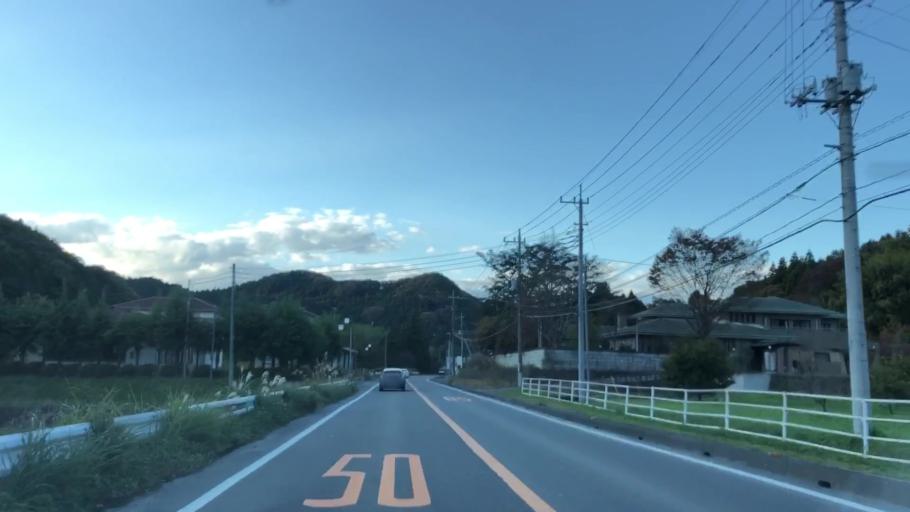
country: JP
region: Ibaraki
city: Kasama
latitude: 36.4817
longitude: 140.2931
